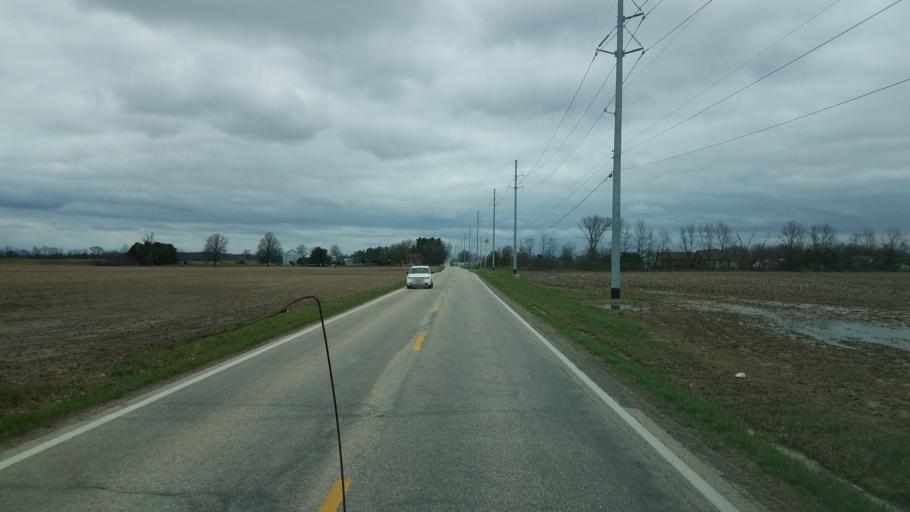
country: US
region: Ohio
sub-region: Delaware County
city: Delaware
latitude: 40.3360
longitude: -83.0996
